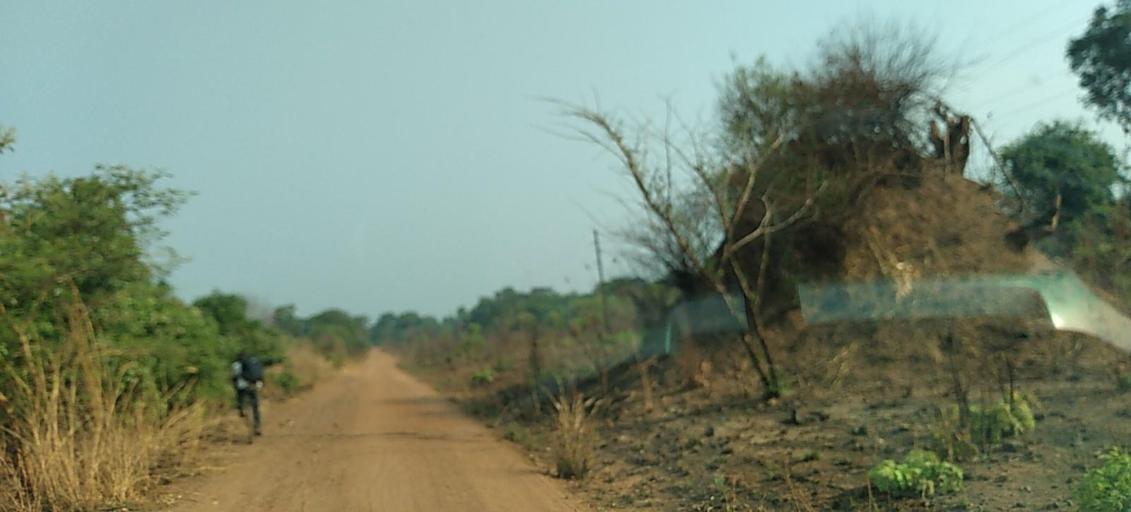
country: ZM
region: Copperbelt
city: Chingola
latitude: -12.8440
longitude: 27.5476
